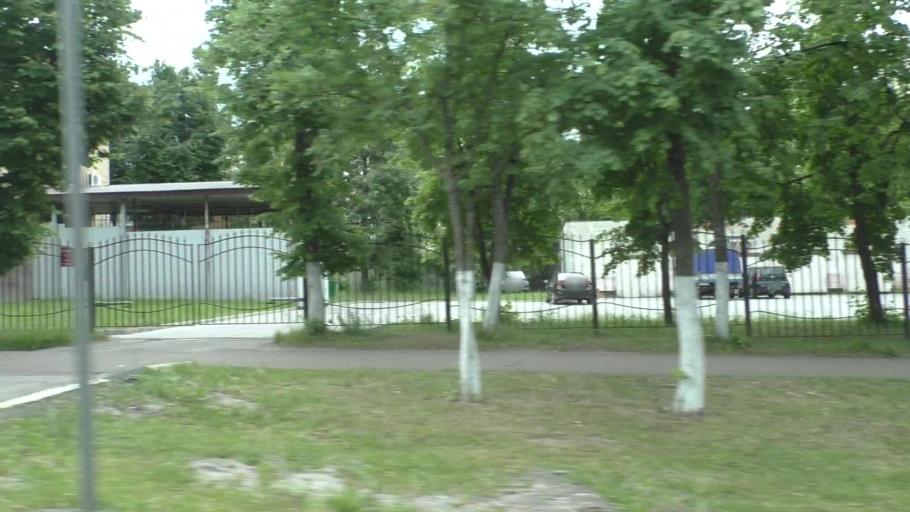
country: RU
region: Moskovskaya
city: Yegor'yevsk
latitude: 55.3718
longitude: 39.0546
